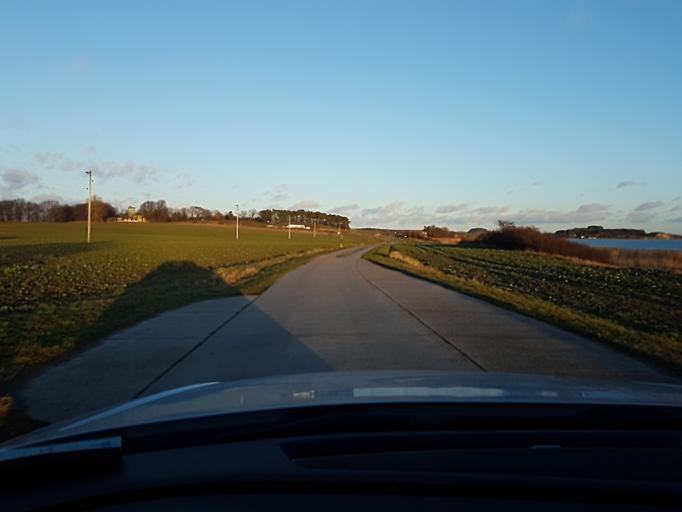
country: DE
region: Mecklenburg-Vorpommern
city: Ostseebad Sellin
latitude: 54.3272
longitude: 13.6556
